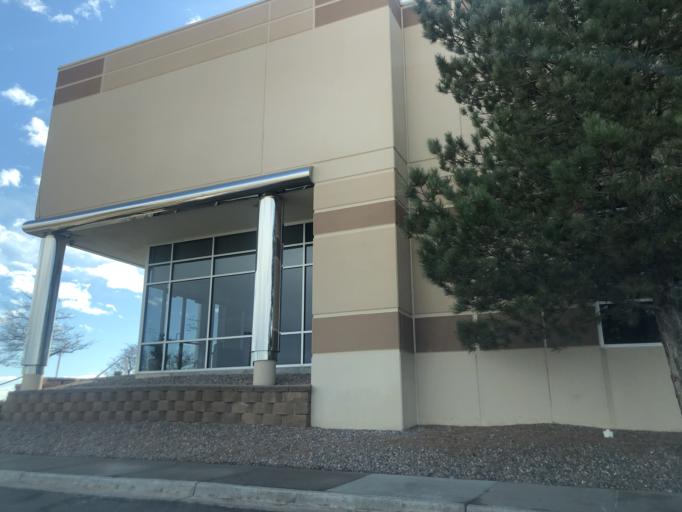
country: US
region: Colorado
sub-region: Douglas County
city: Meridian
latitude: 39.5595
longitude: -104.8551
